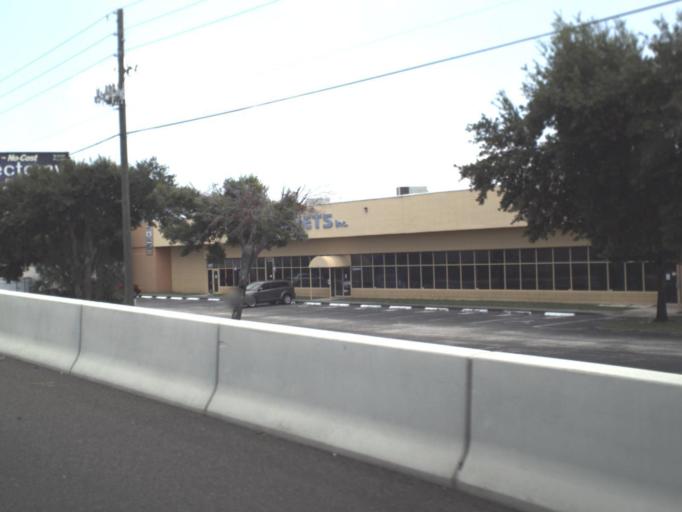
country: US
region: Florida
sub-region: Pinellas County
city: Pinellas Park
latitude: 27.8692
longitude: -82.7049
